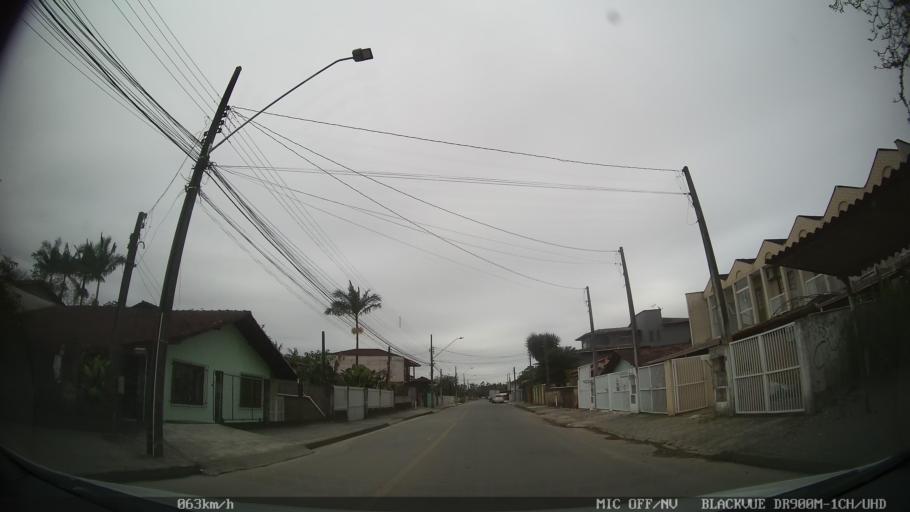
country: BR
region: Santa Catarina
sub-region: Joinville
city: Joinville
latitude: -26.2944
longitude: -48.9096
